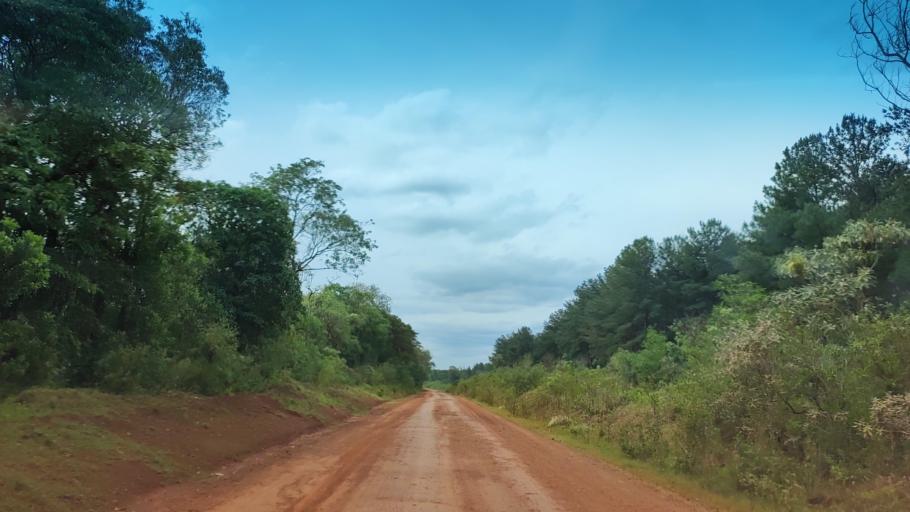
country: AR
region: Misiones
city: Garupa
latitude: -27.5101
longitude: -55.9704
